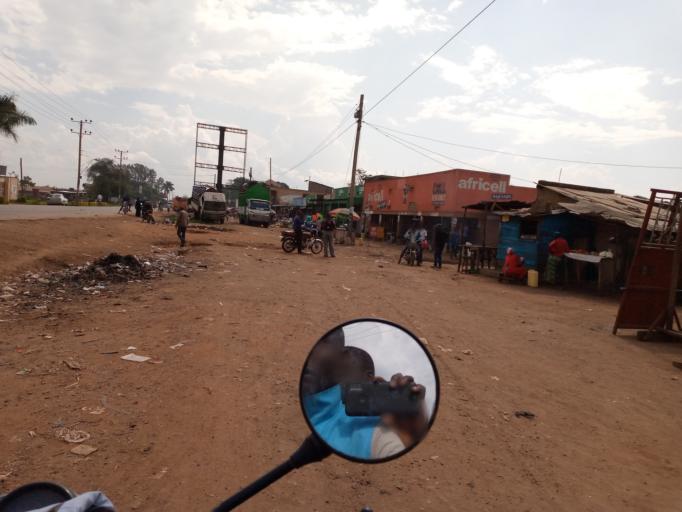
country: UG
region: Eastern Region
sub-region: Mbale District
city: Mbale
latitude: 1.0795
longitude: 34.1628
